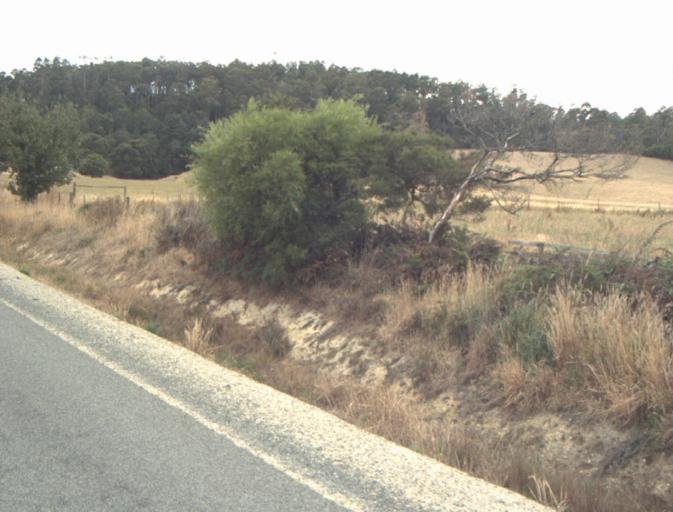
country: AU
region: Tasmania
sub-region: Launceston
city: Mayfield
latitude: -41.2039
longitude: 147.1888
